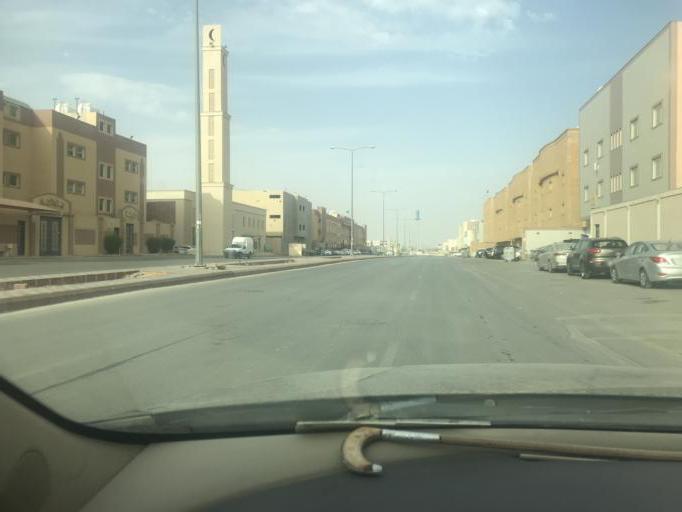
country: SA
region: Ar Riyad
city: Riyadh
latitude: 24.8013
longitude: 46.6698
